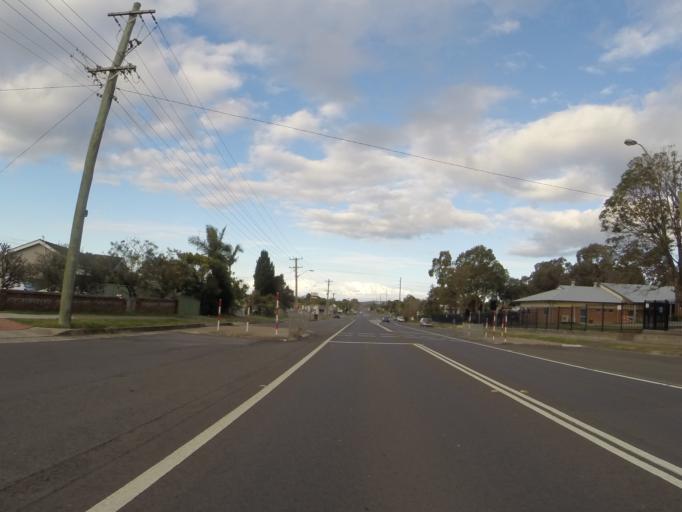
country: AU
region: New South Wales
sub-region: Shellharbour
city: Albion Park Rail
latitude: -34.5716
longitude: 150.7638
